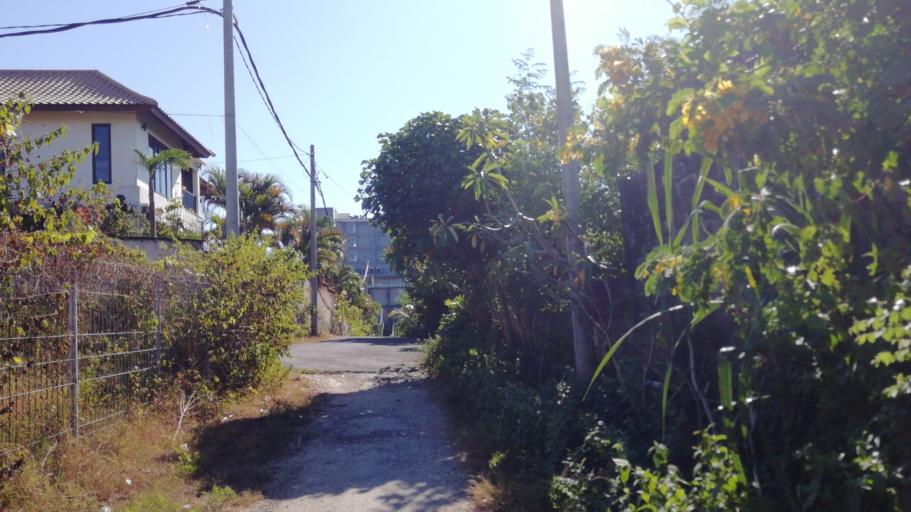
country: ID
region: Bali
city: Jimbaran
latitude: -8.8093
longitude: 115.1609
